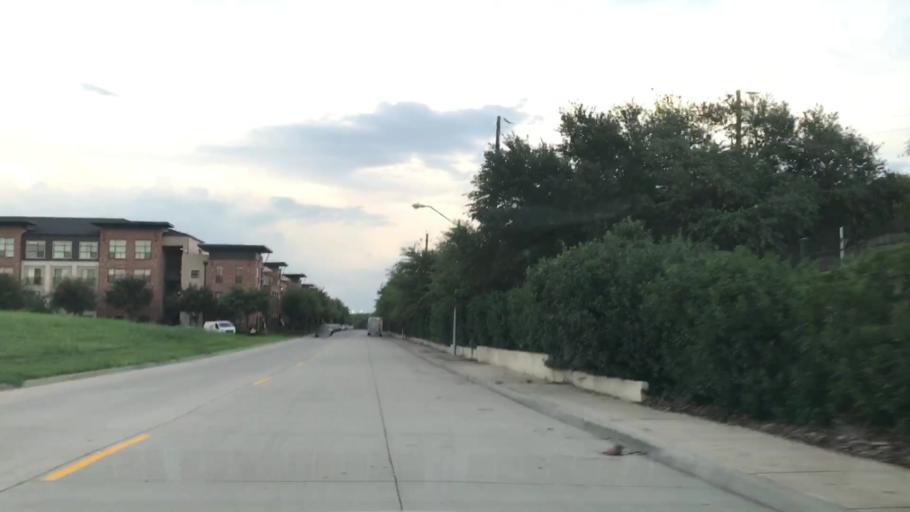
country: US
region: Texas
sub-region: Dallas County
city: Addison
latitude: 33.0110
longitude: -96.8273
